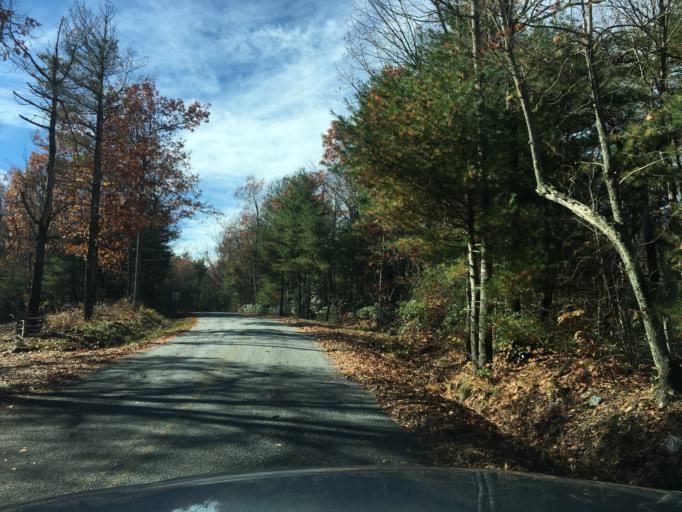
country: US
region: North Carolina
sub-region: Henderson County
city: Valley Hill
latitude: 35.2339
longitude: -82.5125
